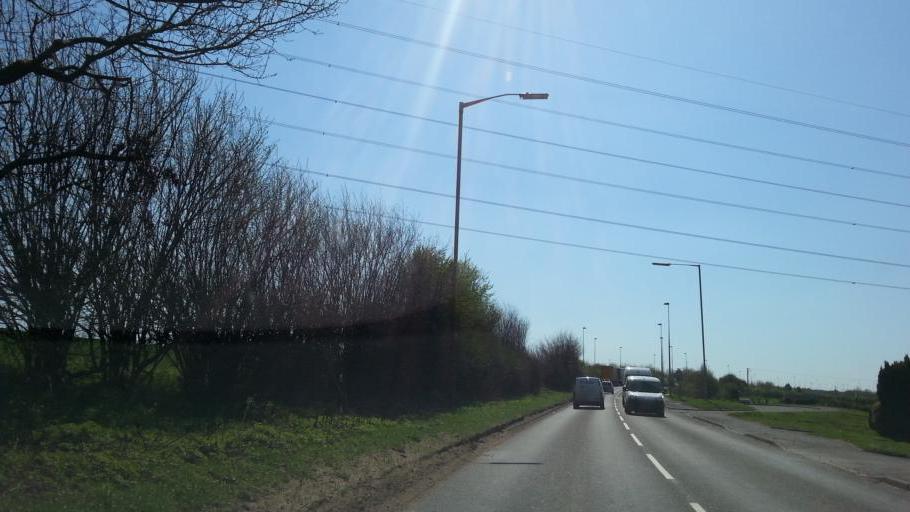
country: GB
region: England
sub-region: Staffordshire
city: Cannock
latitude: 52.6718
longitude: -2.0513
